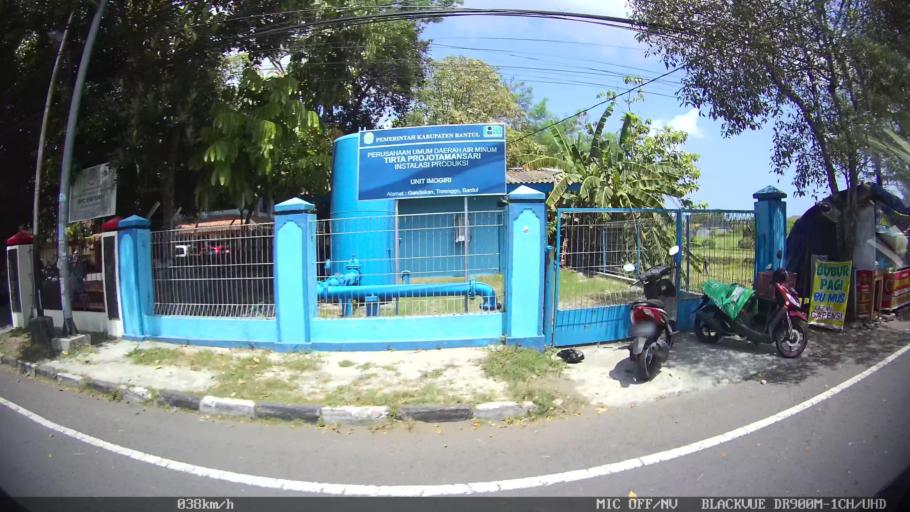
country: ID
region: Daerah Istimewa Yogyakarta
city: Bantul
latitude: -7.8946
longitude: 110.3454
